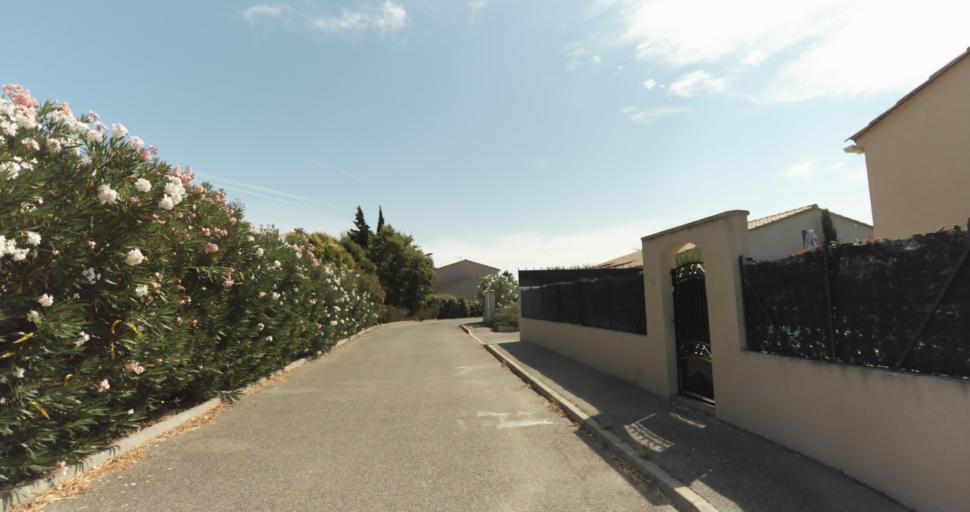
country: FR
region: Provence-Alpes-Cote d'Azur
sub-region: Departement du Vaucluse
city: Monteux
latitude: 44.0358
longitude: 4.9847
